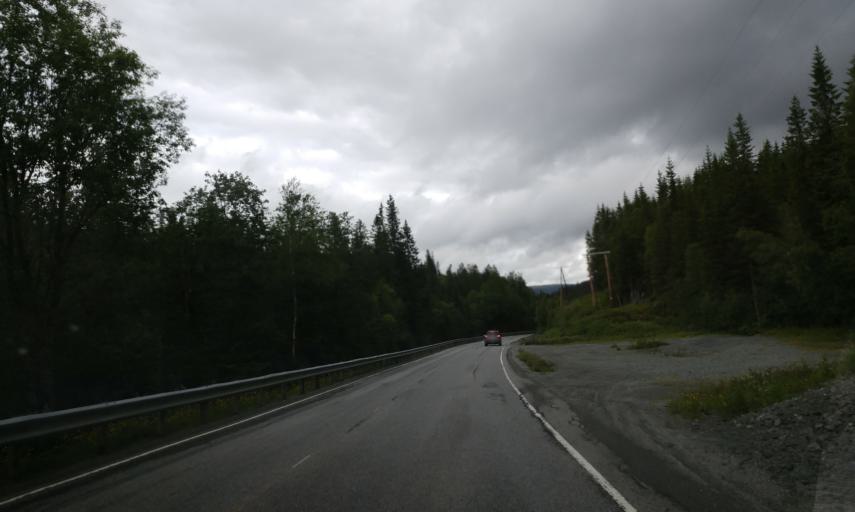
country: NO
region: Sor-Trondelag
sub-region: Selbu
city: Mebonden
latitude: 63.3445
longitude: 11.0767
